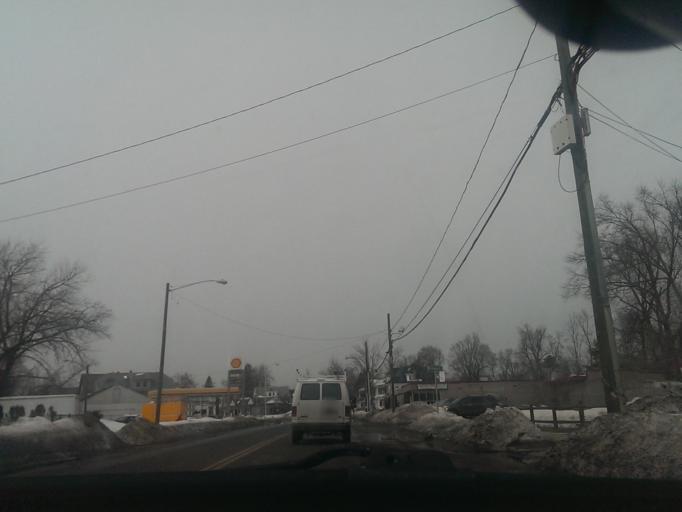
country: US
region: Massachusetts
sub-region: Hampden County
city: East Longmeadow
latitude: 42.0828
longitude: -72.5425
